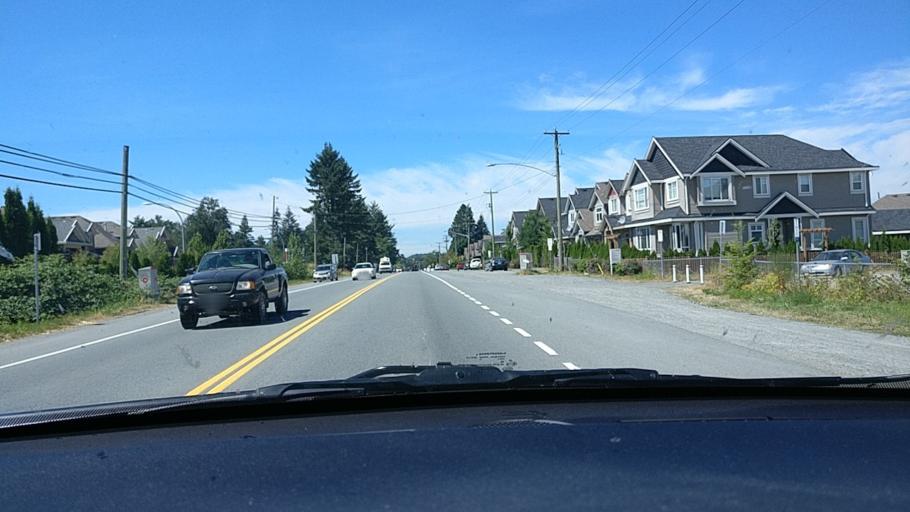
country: CA
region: British Columbia
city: Aldergrove
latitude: 49.0575
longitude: -122.4541
